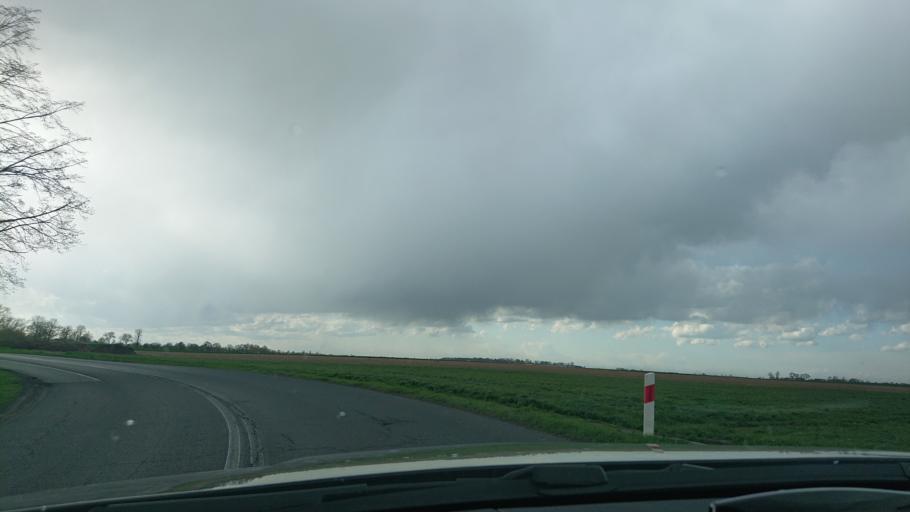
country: PL
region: Greater Poland Voivodeship
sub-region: Powiat gnieznienski
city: Gniezno
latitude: 52.5696
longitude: 17.5229
